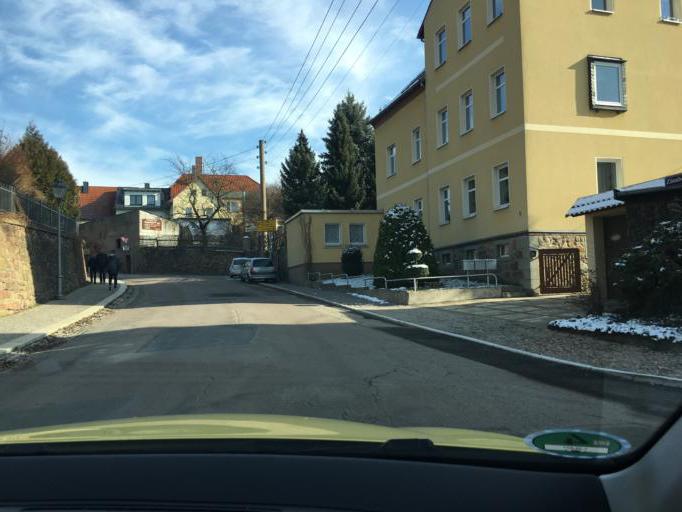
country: DE
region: Saxony
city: Penig
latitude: 50.9304
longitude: 12.7043
